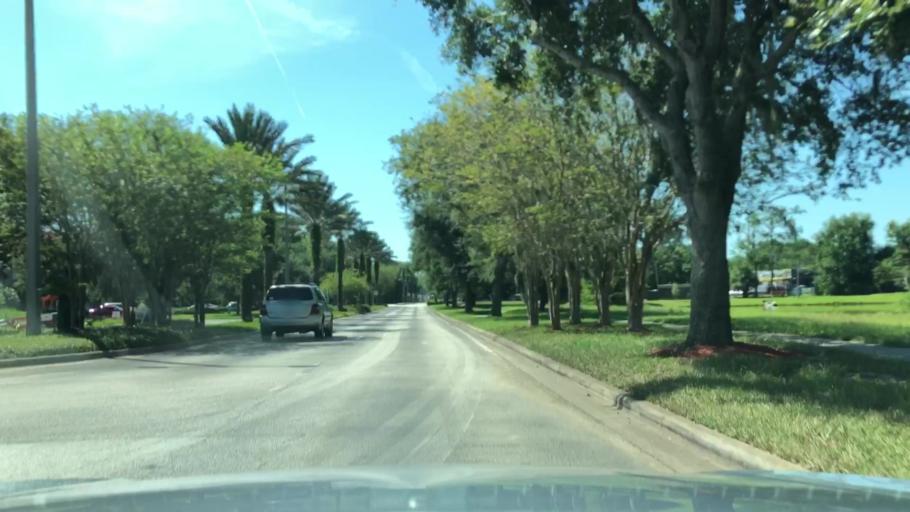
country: US
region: Florida
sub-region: Saint Johns County
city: Saint Augustine
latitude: 29.9193
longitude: -81.4089
